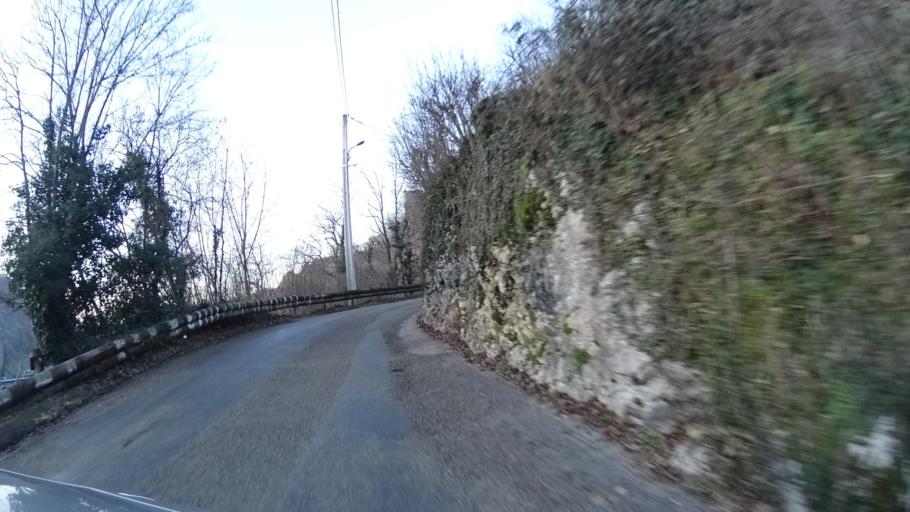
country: FR
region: Franche-Comte
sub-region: Departement du Doubs
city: Besancon
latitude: 47.2249
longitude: 6.0344
